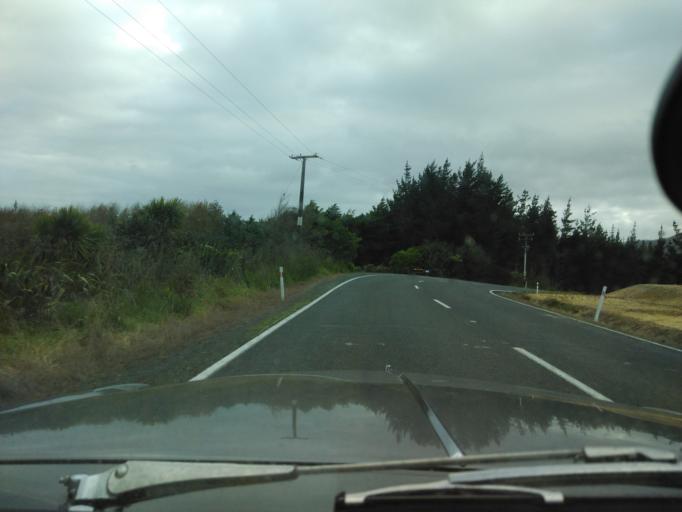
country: NZ
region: Auckland
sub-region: Auckland
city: Wellsford
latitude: -36.1738
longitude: 174.4168
